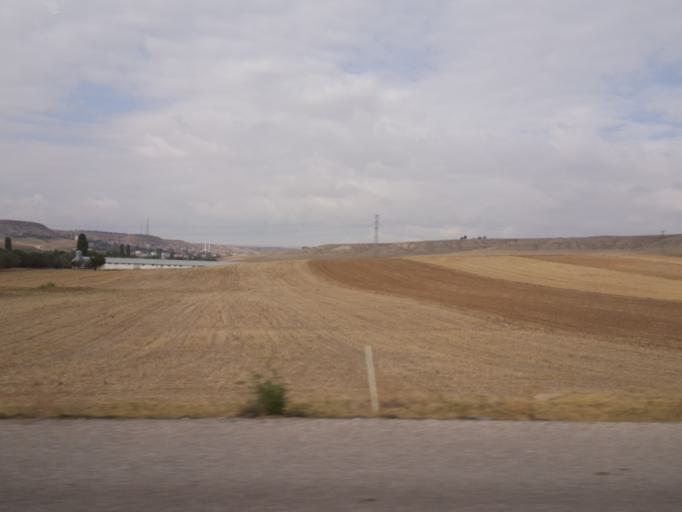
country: TR
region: Kirikkale
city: Karakecili
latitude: 39.5865
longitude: 33.4096
